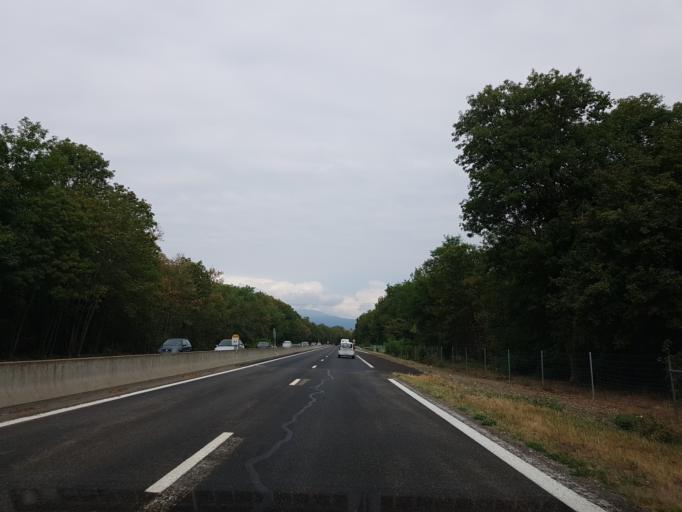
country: FR
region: Alsace
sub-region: Departement du Haut-Rhin
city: Pulversheim
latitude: 47.8286
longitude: 7.2828
